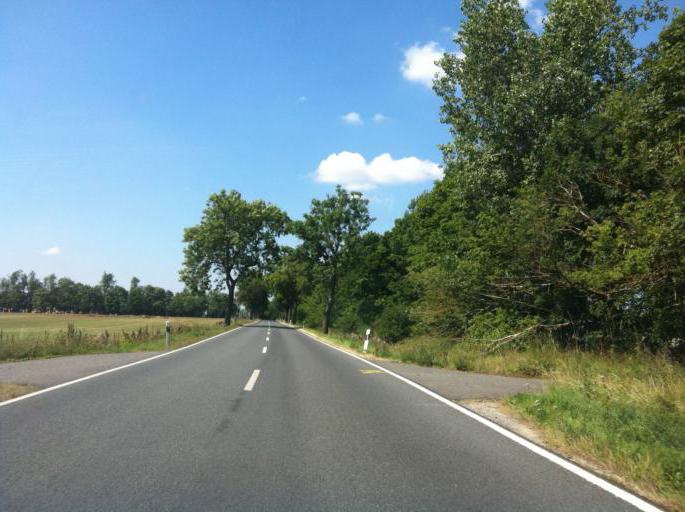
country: DE
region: Thuringia
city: Kefferhausen
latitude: 51.3359
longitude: 10.2761
